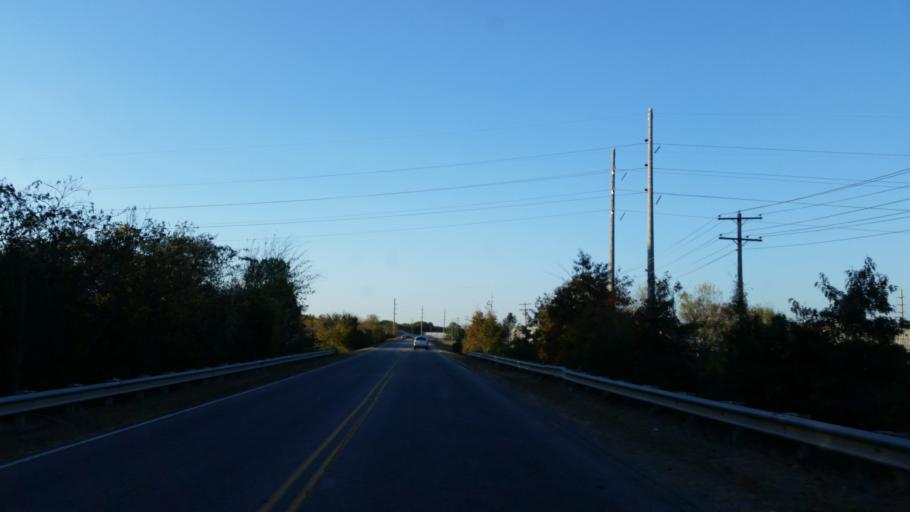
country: US
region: Georgia
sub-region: Gordon County
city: Calhoun
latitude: 34.4838
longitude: -84.9538
